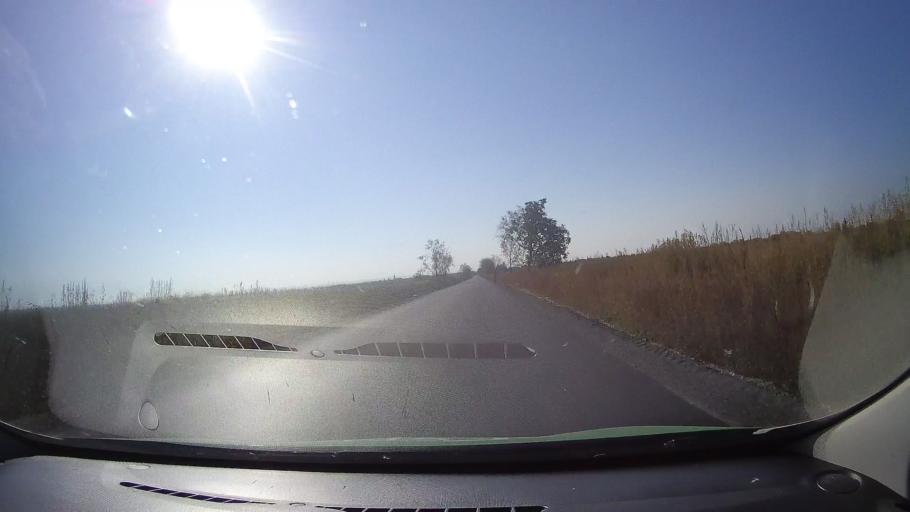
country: RO
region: Satu Mare
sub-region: Comuna Tiream
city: Tiream
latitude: 47.6296
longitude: 22.4674
